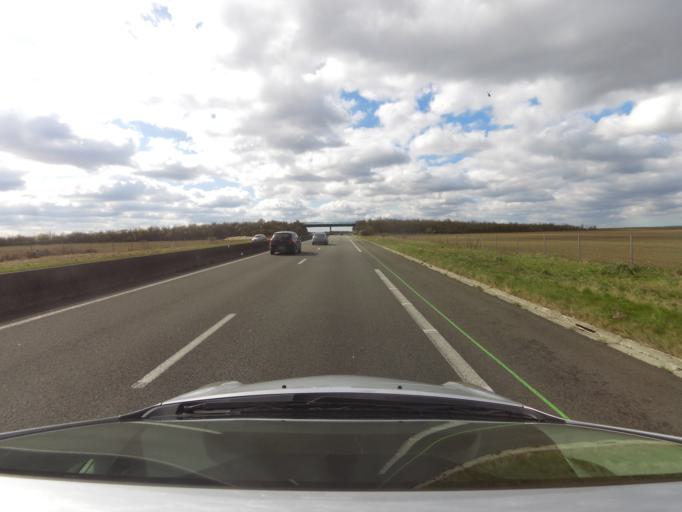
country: FR
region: Picardie
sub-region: Departement de la Somme
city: Sailly-Flibeaucourt
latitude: 50.1868
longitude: 1.7554
